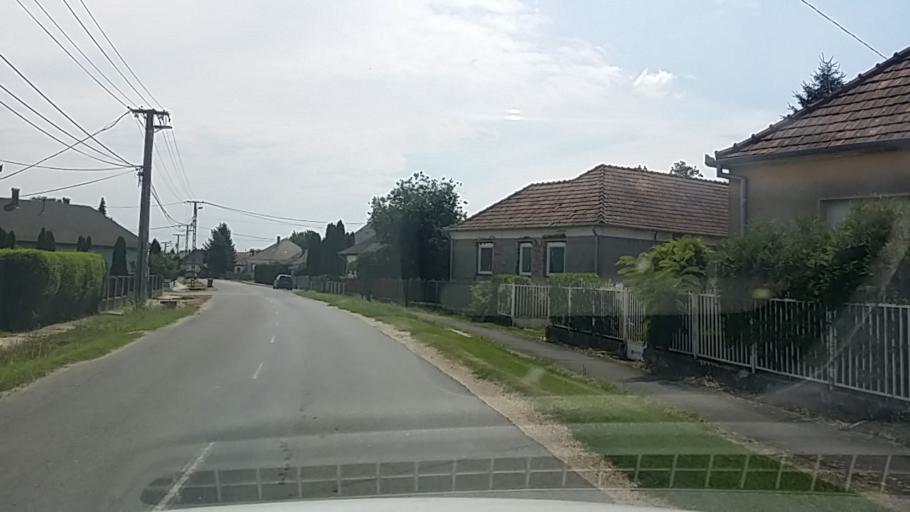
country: HU
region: Zala
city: Becsehely
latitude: 46.4019
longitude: 16.7903
